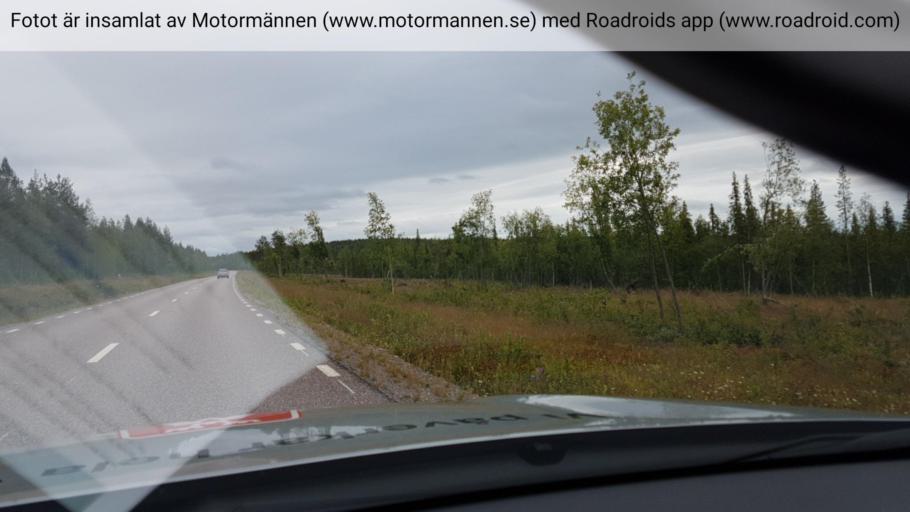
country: SE
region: Norrbotten
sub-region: Gallivare Kommun
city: Gaellivare
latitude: 67.0433
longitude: 21.6389
